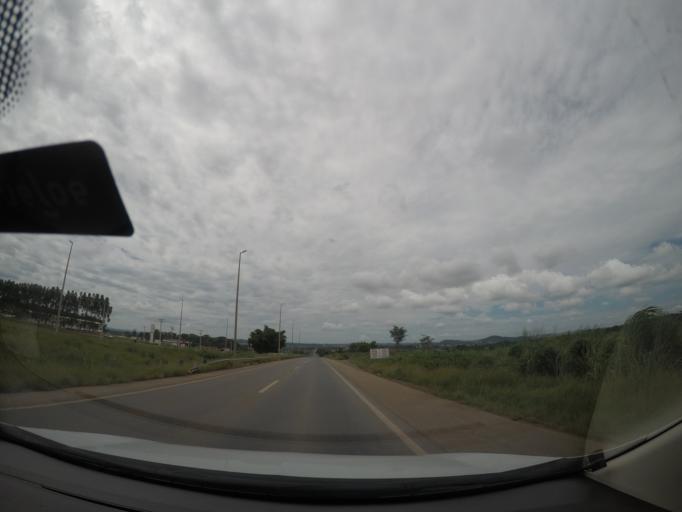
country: BR
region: Goias
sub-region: Goianira
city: Goianira
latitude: -16.4656
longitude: -49.4406
